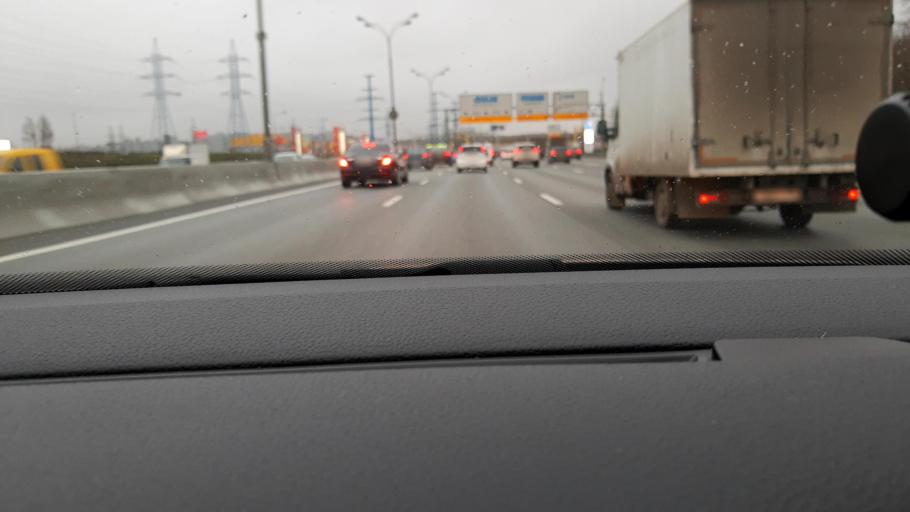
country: RU
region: Moscow
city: Lianozovo
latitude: 55.9105
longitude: 37.5741
